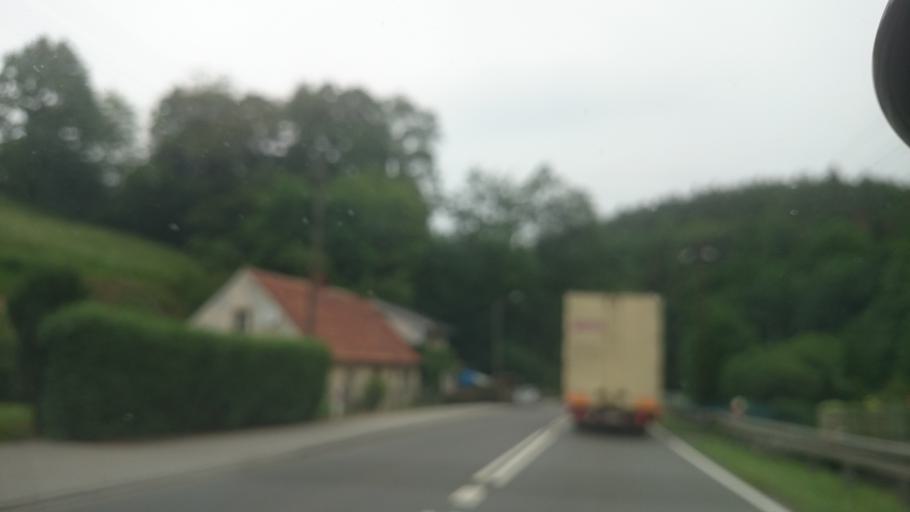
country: PL
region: Lower Silesian Voivodeship
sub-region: Powiat zabkowicki
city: Zloty Stok
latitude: 50.4477
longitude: 16.8378
